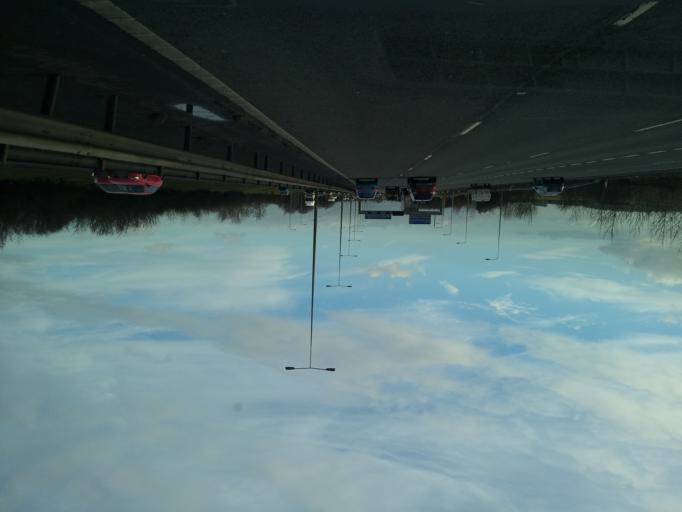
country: GB
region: England
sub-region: Cambridgeshire
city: Stilton
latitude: 52.5255
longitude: -0.3102
